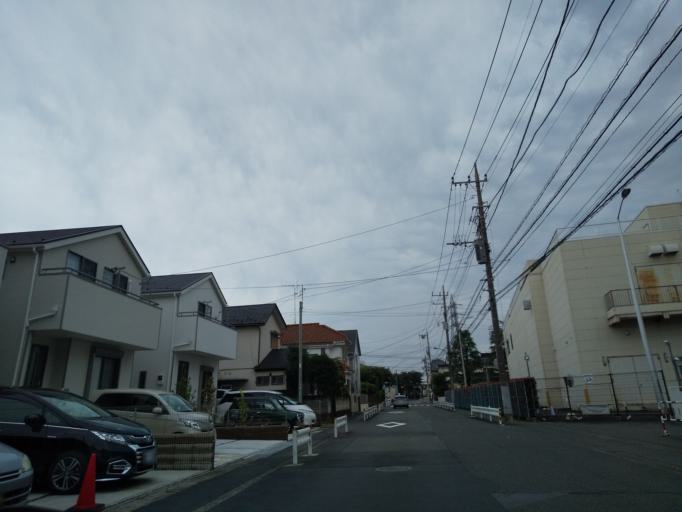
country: JP
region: Tokyo
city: Hino
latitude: 35.6708
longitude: 139.3716
